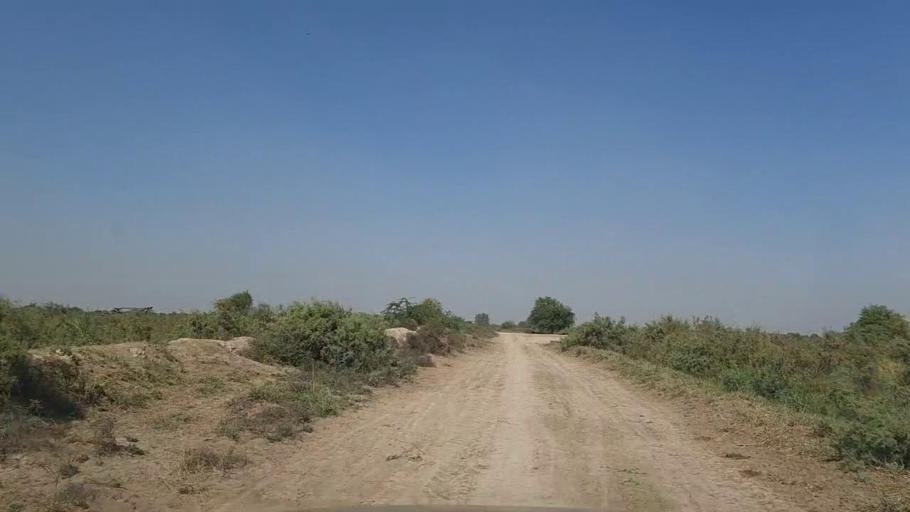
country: PK
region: Sindh
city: Daro Mehar
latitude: 24.8236
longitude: 68.1504
